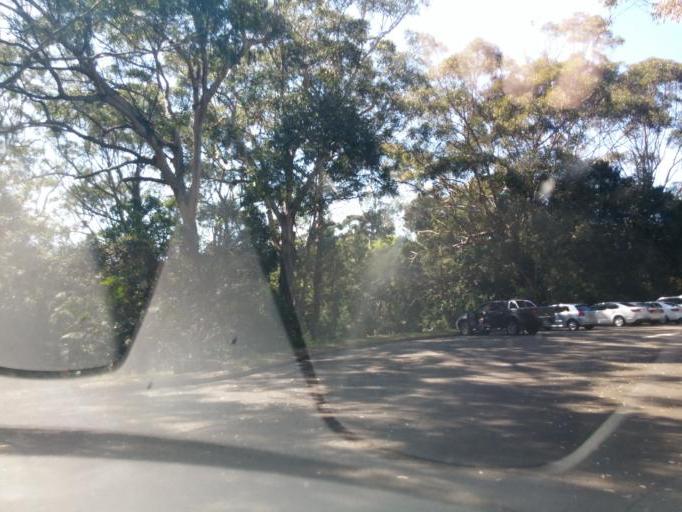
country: AU
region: New South Wales
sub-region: Port Macquarie-Hastings
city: Port Macquarie
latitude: -31.4606
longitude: 152.9296
